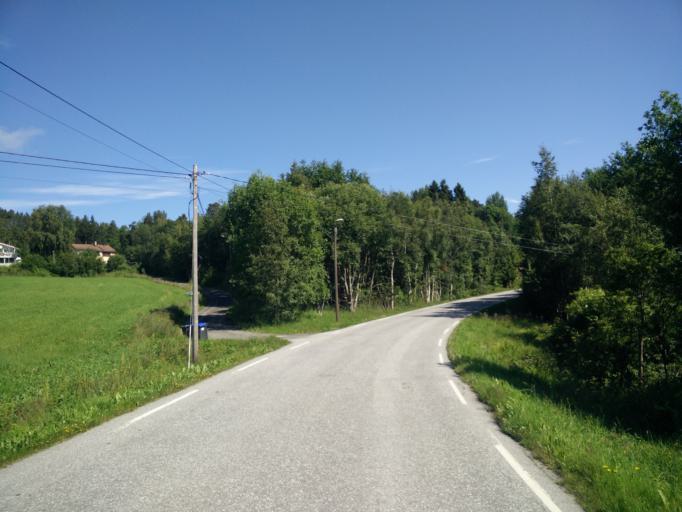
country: NO
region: More og Romsdal
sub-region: Kristiansund
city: Rensvik
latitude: 63.0494
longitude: 7.8590
